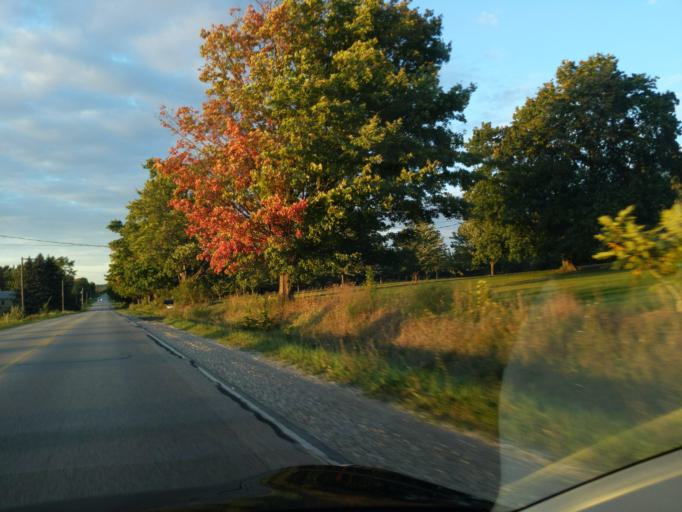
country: US
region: Michigan
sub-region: Antrim County
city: Elk Rapids
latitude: 44.8397
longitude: -85.4053
